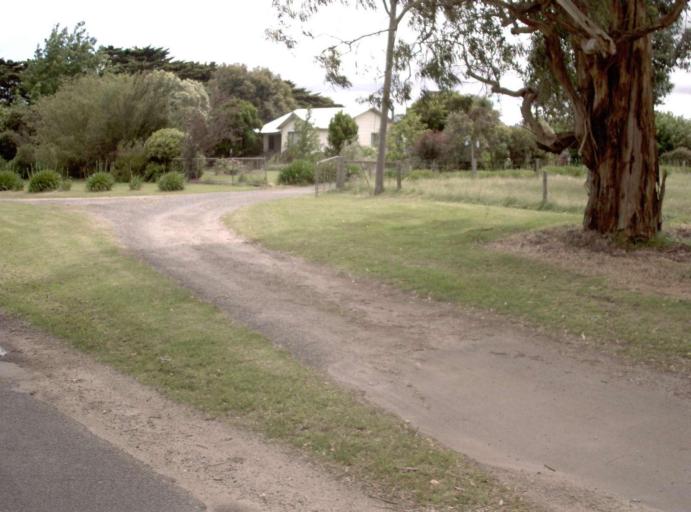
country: AU
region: Victoria
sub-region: Latrobe
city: Moe
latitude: -38.0091
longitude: 146.1481
